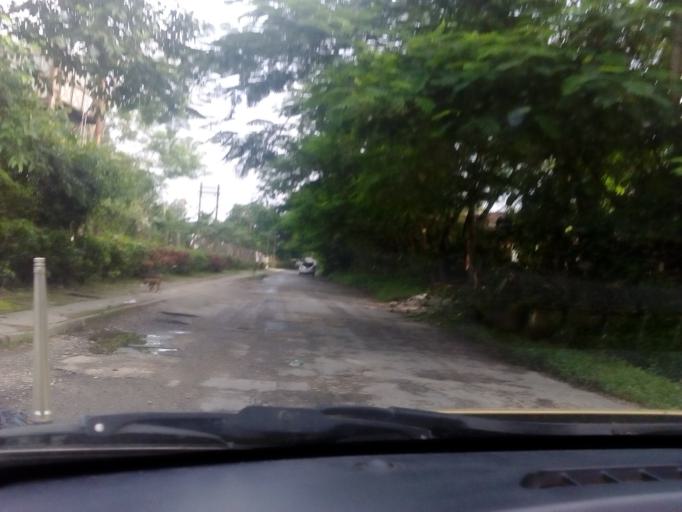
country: MM
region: Yangon
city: Yangon
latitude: 16.8452
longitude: 96.1526
